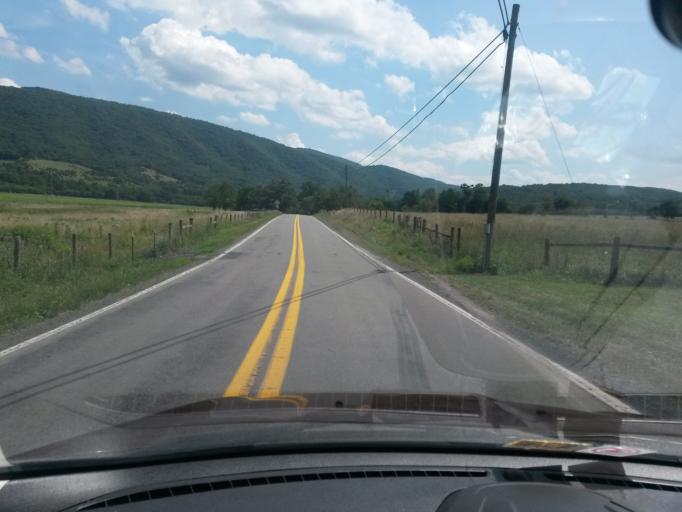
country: US
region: West Virginia
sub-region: Pendleton County
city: Franklin
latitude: 38.7592
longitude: -79.2886
